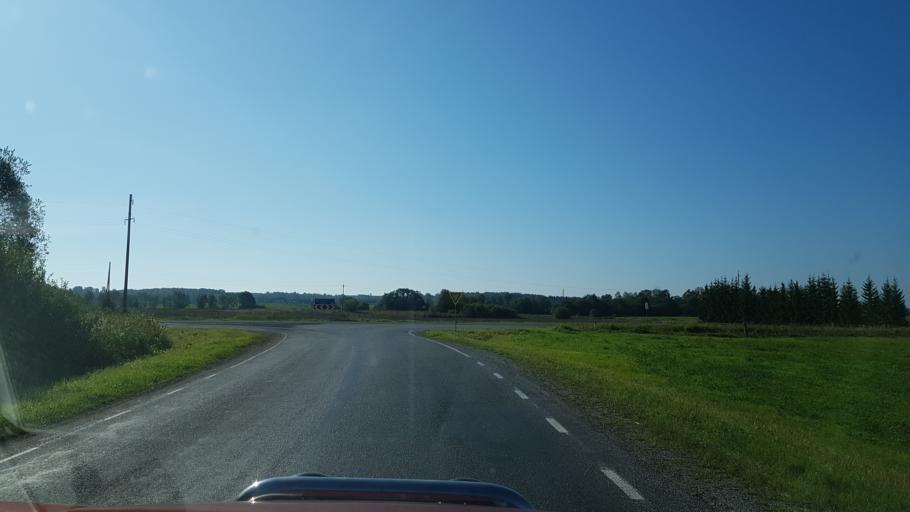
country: EE
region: Jogevamaa
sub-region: Jogeva linn
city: Jogeva
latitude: 58.5823
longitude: 26.3081
